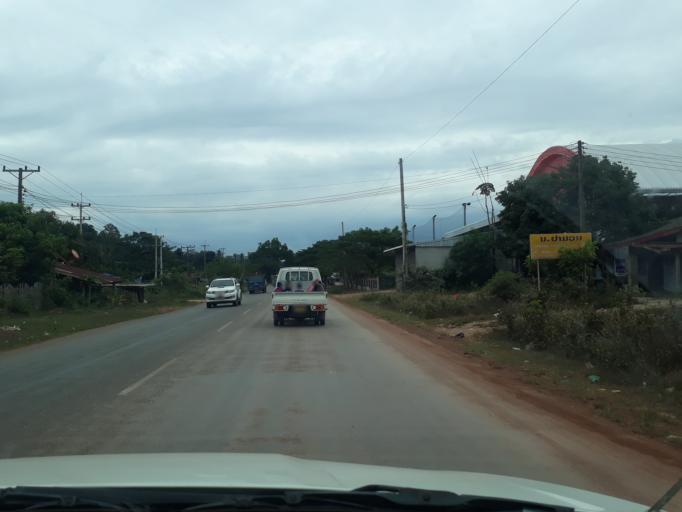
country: LA
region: Vientiane
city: Muang Phon-Hong
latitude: 18.3332
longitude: 102.4402
